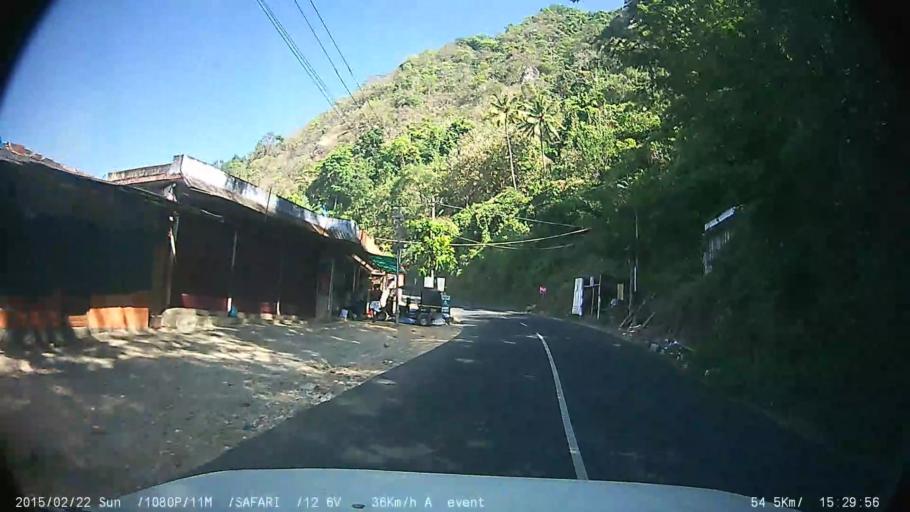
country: IN
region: Kerala
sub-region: Kottayam
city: Erattupetta
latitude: 9.5589
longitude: 76.9507
